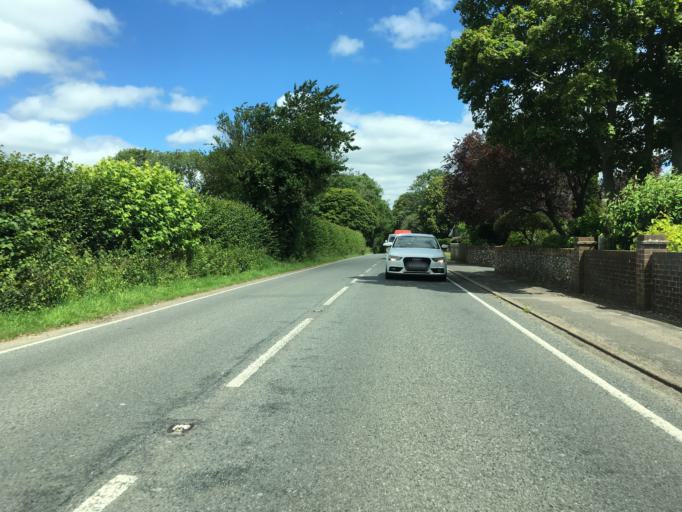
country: GB
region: England
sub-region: Hampshire
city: Highclere
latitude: 51.3387
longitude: -1.3755
